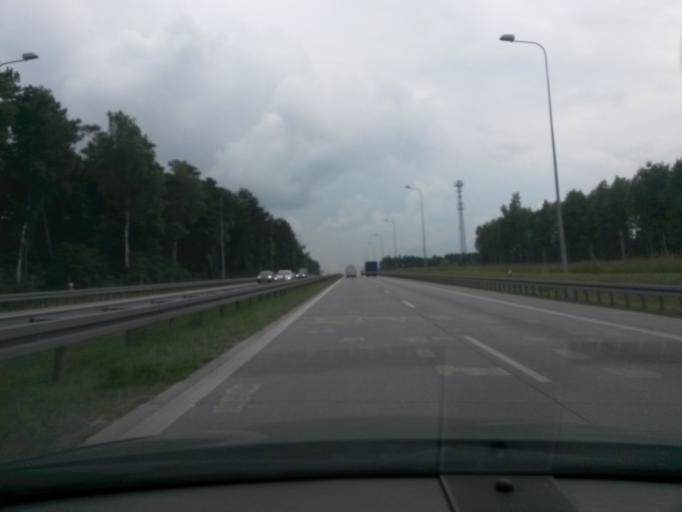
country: PL
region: Lodz Voivodeship
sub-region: Powiat rawski
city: Rawa Mazowiecka
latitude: 51.8233
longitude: 20.3214
